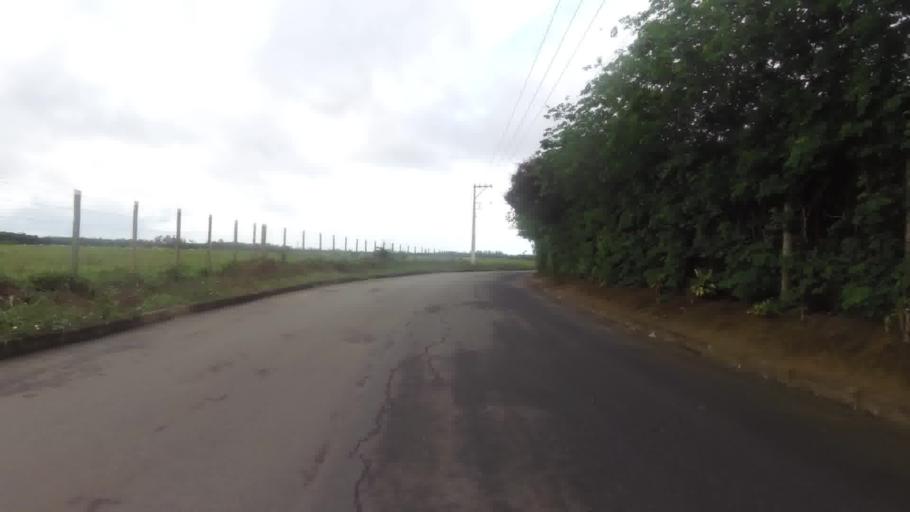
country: BR
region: Espirito Santo
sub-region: Piuma
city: Piuma
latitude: -20.7695
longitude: -40.6299
